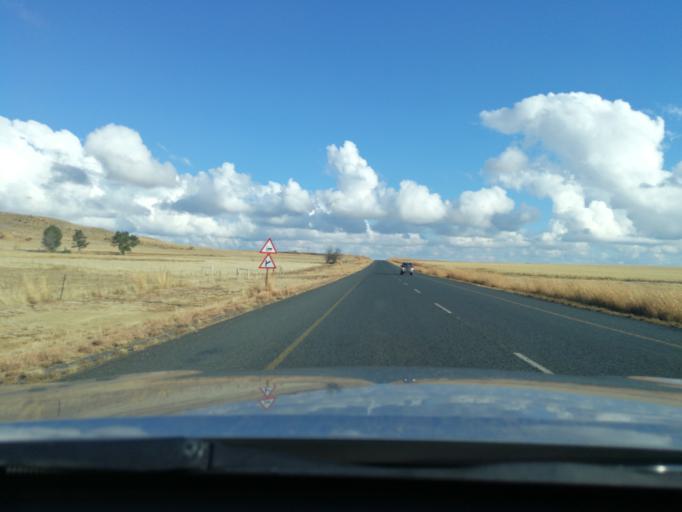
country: ZA
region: Orange Free State
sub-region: Thabo Mofutsanyana District Municipality
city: Bethlehem
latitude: -28.0782
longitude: 28.3582
